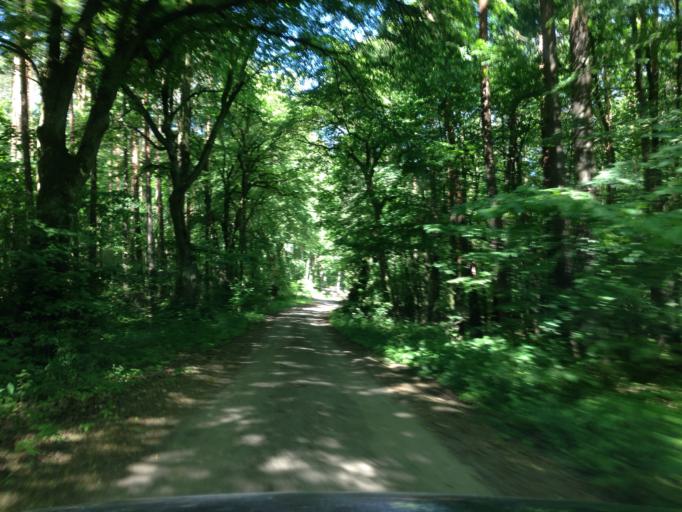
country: PL
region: Kujawsko-Pomorskie
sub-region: Powiat brodnicki
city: Bartniczka
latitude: 53.2637
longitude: 19.5808
